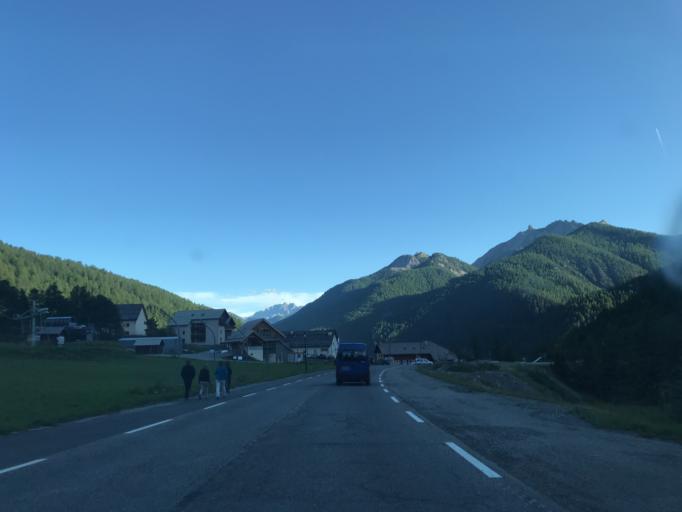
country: FR
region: Provence-Alpes-Cote d'Azur
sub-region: Departement des Hautes-Alpes
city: Villar-Saint-Pancrace
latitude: 44.7833
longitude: 6.7348
